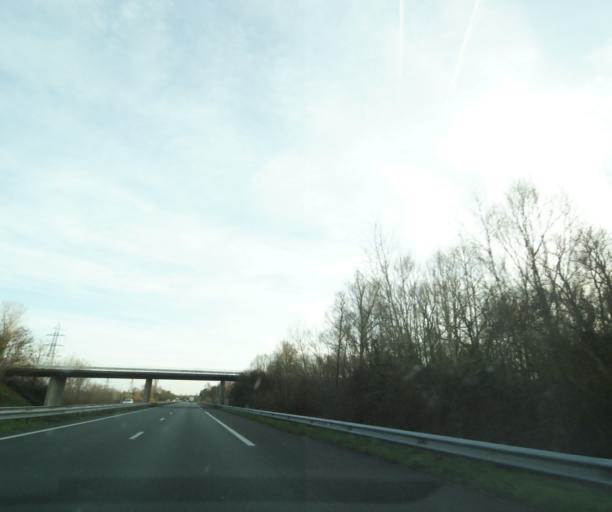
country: FR
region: Aquitaine
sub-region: Departement de la Gironde
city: Pugnac
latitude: 45.0837
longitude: -0.4697
